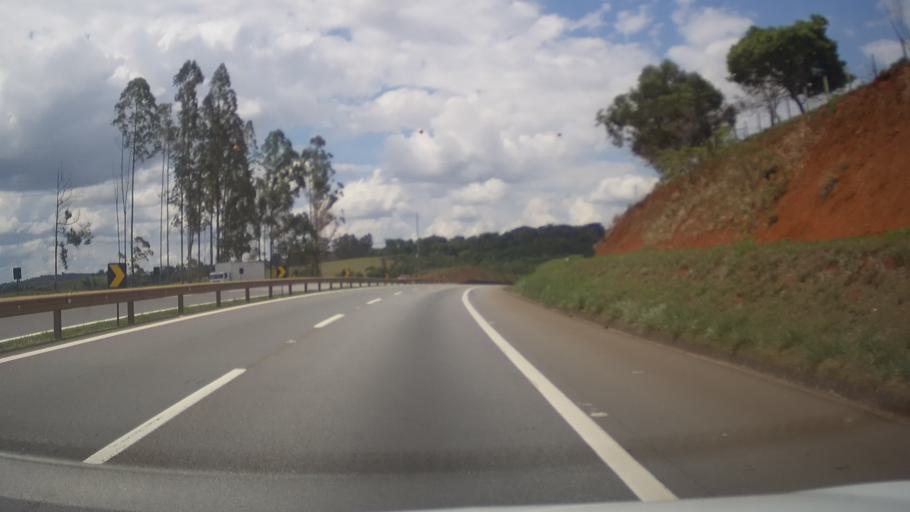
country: BR
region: Minas Gerais
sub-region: Nepomuceno
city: Nepomuceno
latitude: -21.2910
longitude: -45.1479
